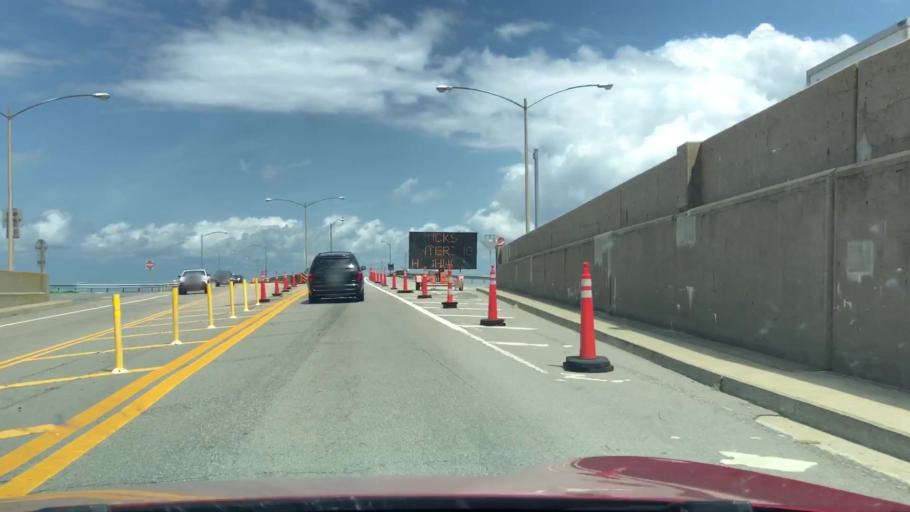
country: US
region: Virginia
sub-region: City of Virginia Beach
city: Virginia Beach
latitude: 36.9837
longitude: -76.1054
